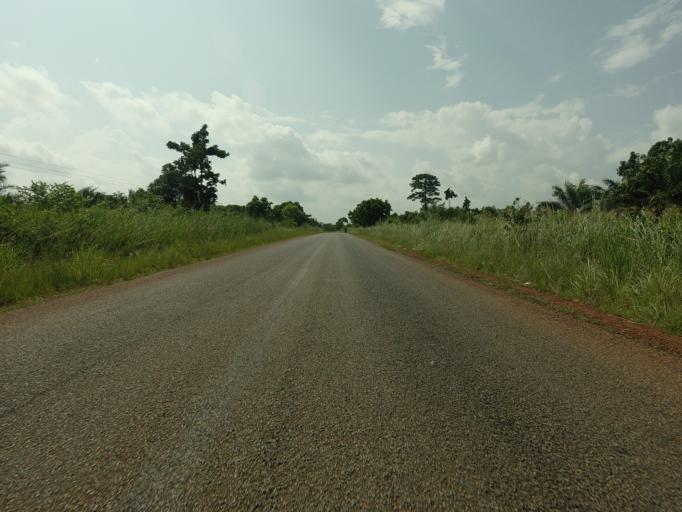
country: TG
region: Maritime
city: Tsevie
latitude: 6.3513
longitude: 0.8709
